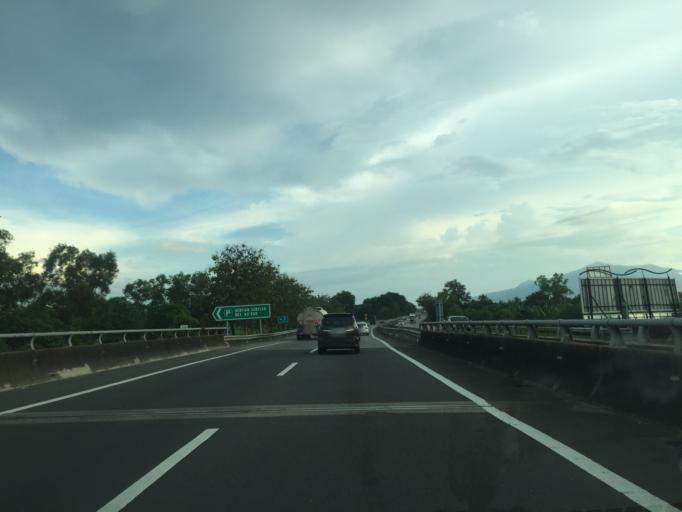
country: MY
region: Kedah
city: Gurun
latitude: 5.9711
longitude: 100.4446
